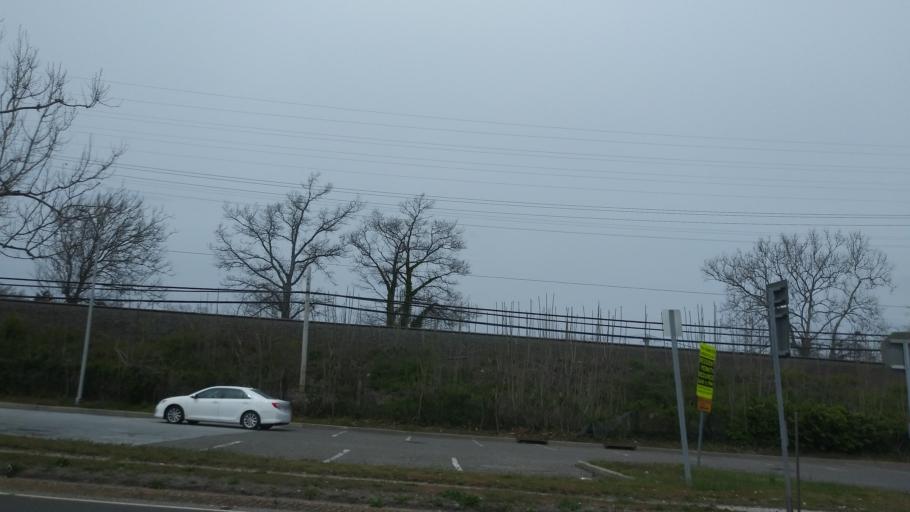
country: US
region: New York
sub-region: Nassau County
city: Baldwin
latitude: 40.6564
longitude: -73.6108
